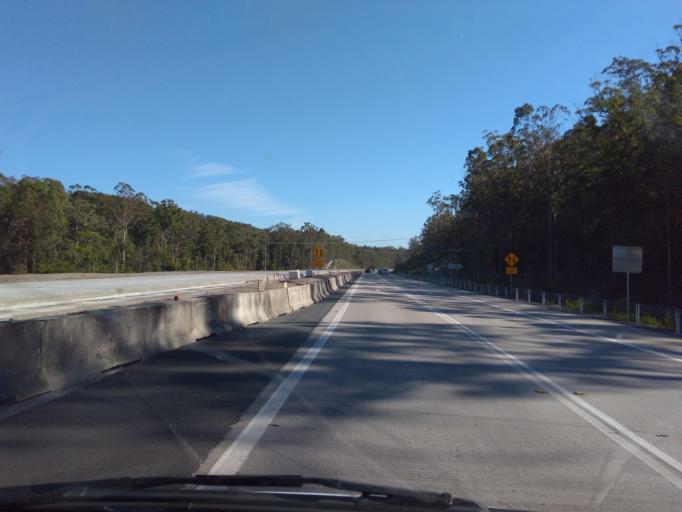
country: AU
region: New South Wales
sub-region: Port Macquarie-Hastings
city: North Shore
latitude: -31.2633
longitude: 152.8142
